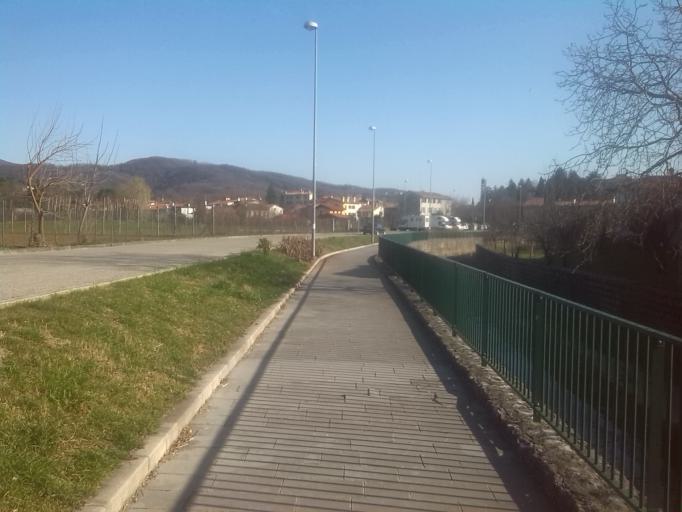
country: IT
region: Friuli Venezia Giulia
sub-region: Provincia di Udine
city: Cividale del Friuli
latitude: 46.0952
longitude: 13.4351
